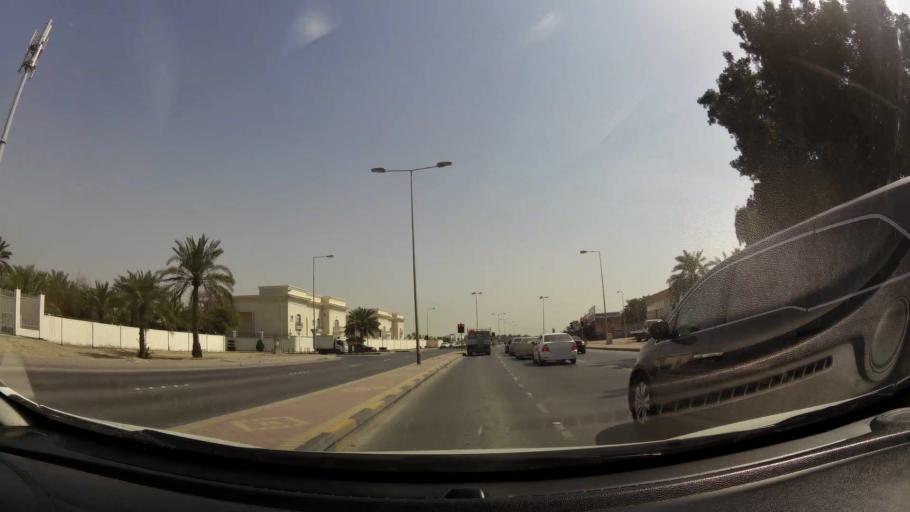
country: BH
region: Northern
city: Madinat `Isa
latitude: 26.1919
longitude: 50.4647
